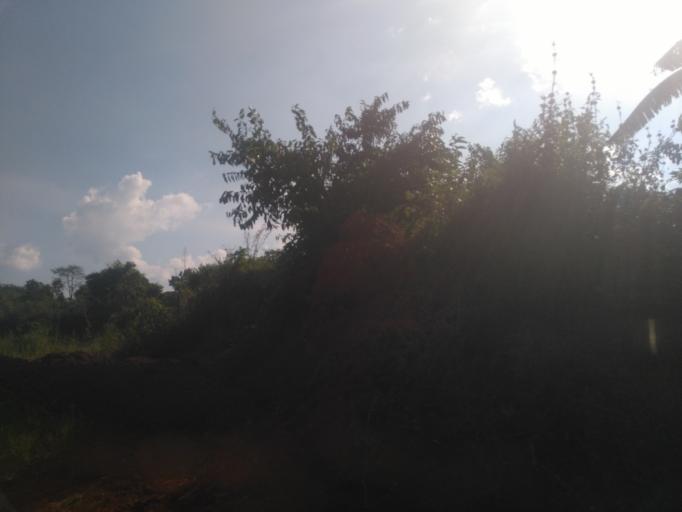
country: UG
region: Central Region
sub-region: Wakiso District
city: Wakiso
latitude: 0.3080
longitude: 32.4444
